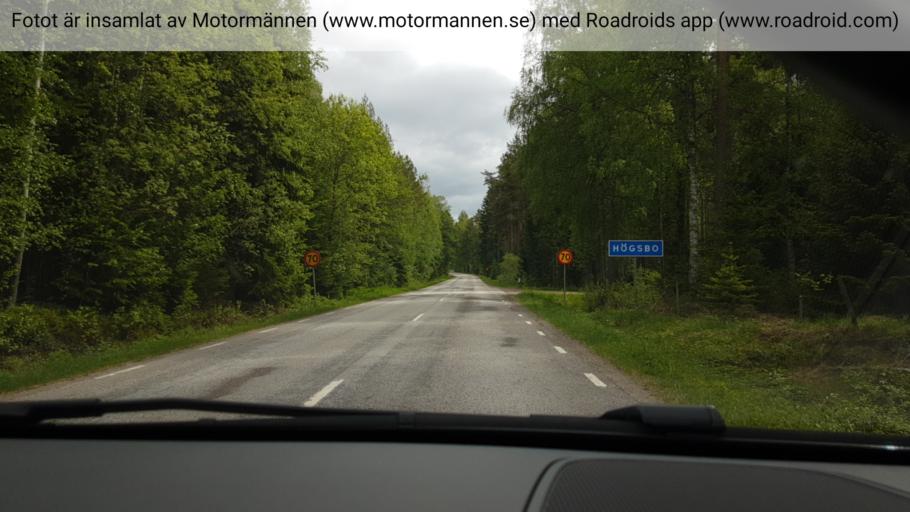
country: SE
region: Uppsala
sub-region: Heby Kommun
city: Tarnsjo
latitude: 60.1203
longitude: 17.0169
